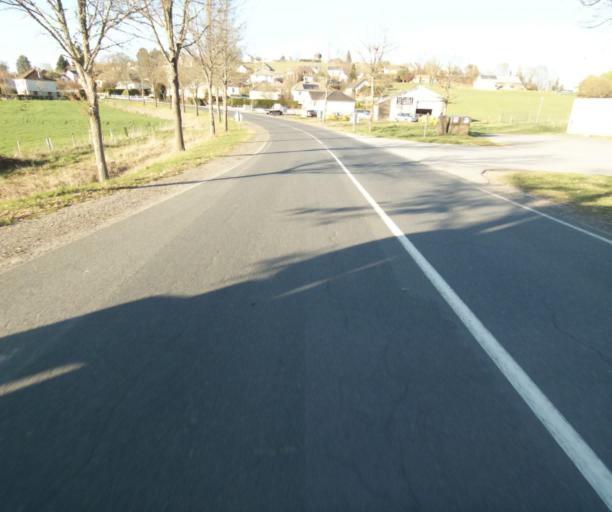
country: FR
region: Limousin
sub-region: Departement de la Correze
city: Seilhac
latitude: 45.3604
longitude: 1.7139
